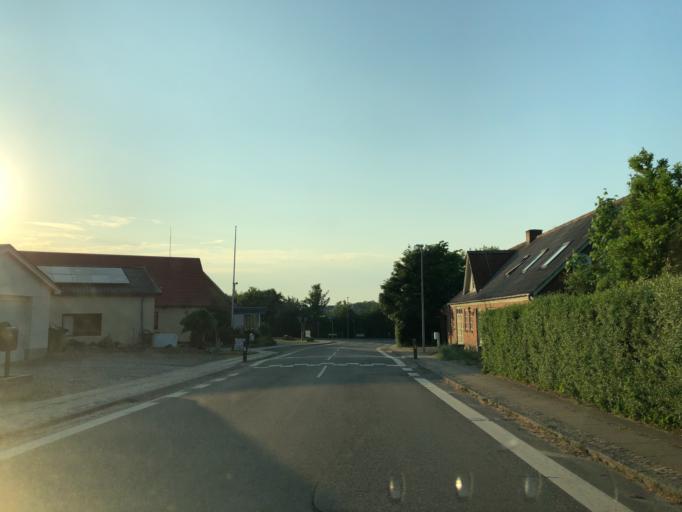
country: DK
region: Central Jutland
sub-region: Struer Kommune
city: Struer
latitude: 56.4335
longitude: 8.5129
